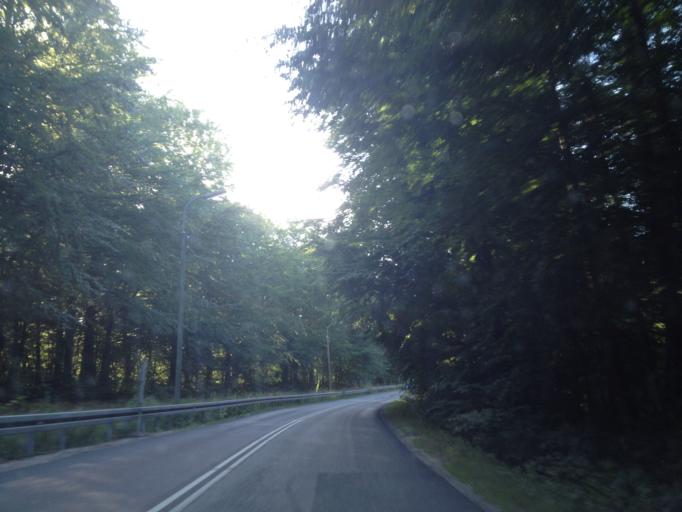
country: DK
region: Capital Region
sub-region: Hillerod Kommune
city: Hillerod
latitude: 55.9480
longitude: 12.2923
